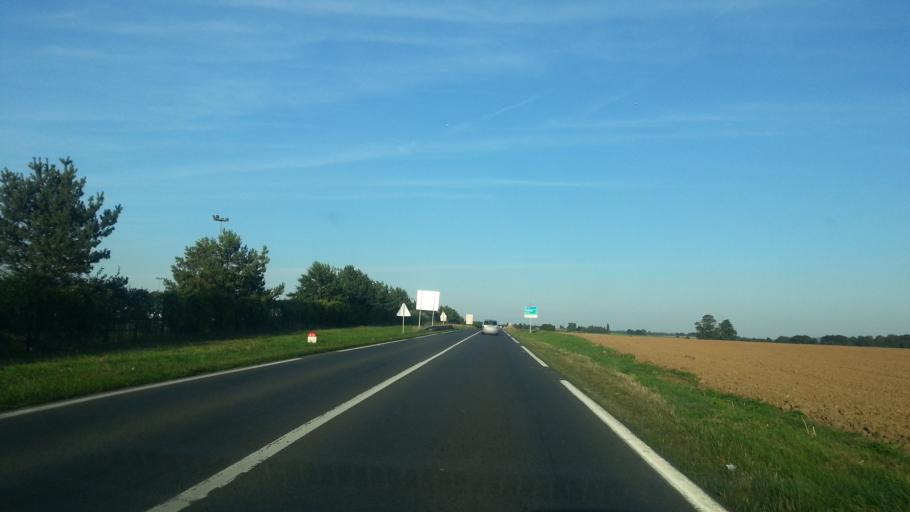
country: FR
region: Picardie
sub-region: Departement de l'Oise
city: Sacy-le-Grand
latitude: 49.3888
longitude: 2.5796
